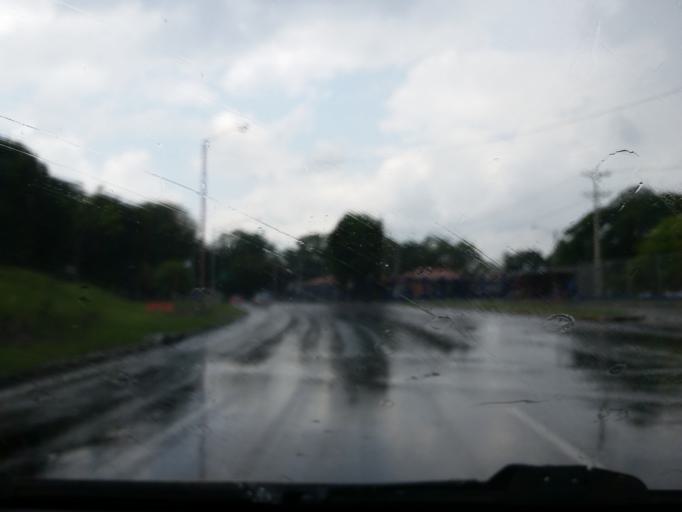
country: PA
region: Panama
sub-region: Distrito de Panama
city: Ancon
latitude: 8.9660
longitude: -79.5509
